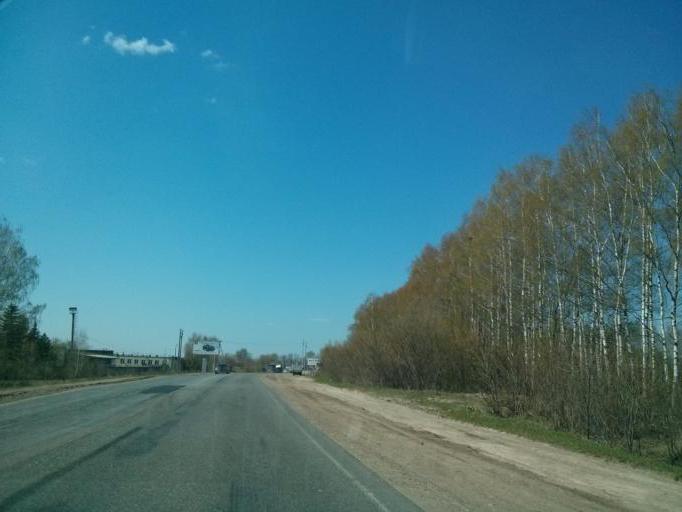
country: RU
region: Nizjnij Novgorod
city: Nizhniy Novgorod
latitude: 56.2169
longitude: 43.9449
